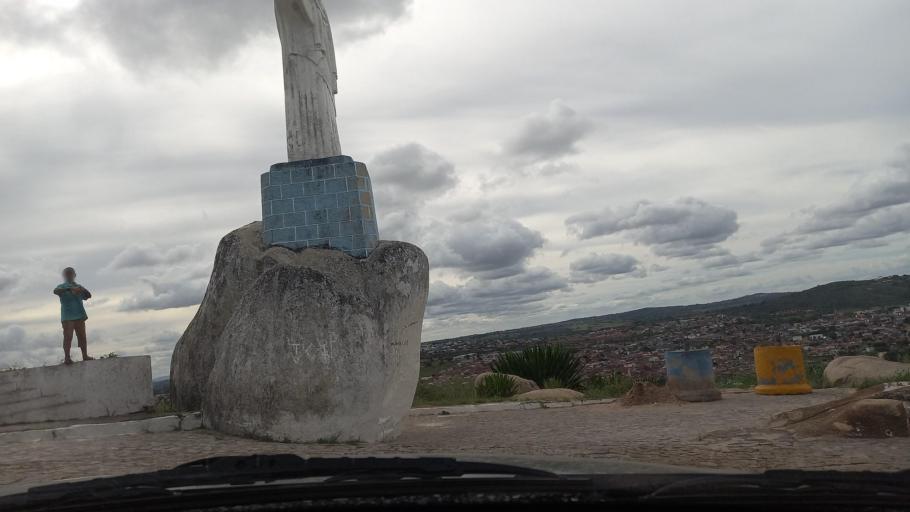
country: BR
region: Pernambuco
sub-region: Gravata
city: Gravata
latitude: -8.2106
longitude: -35.5742
